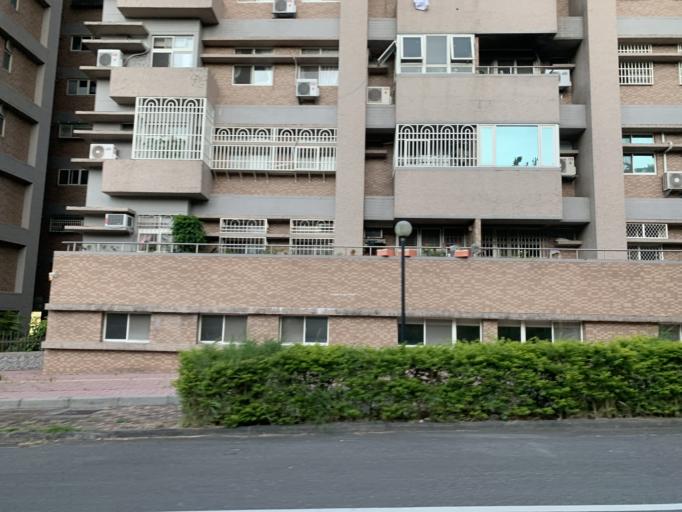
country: TW
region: Taiwan
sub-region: Hualien
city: Hualian
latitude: 23.9998
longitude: 121.6294
